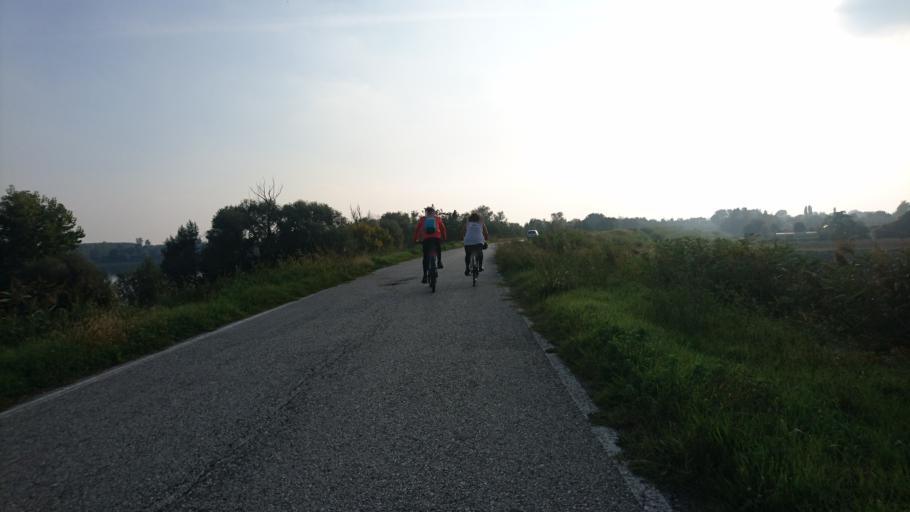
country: IT
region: Veneto
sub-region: Provincia di Rovigo
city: Canaro
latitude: 44.9238
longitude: 11.6989
